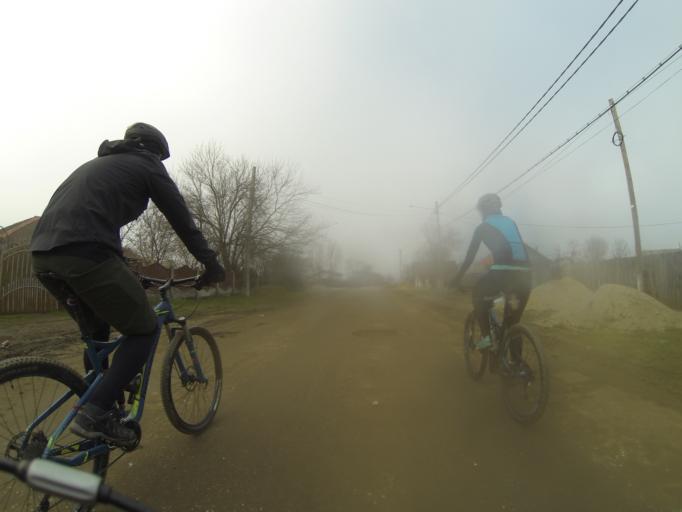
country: RO
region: Mehedinti
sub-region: Comuna Baclesu
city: Baclesu
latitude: 44.4778
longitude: 23.1117
